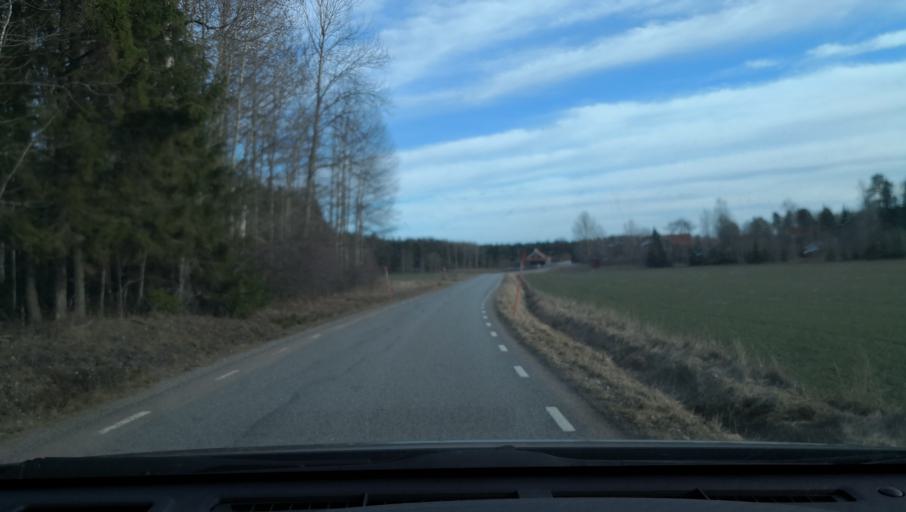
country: SE
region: Uppsala
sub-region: Enkopings Kommun
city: Grillby
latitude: 59.5427
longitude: 17.1623
